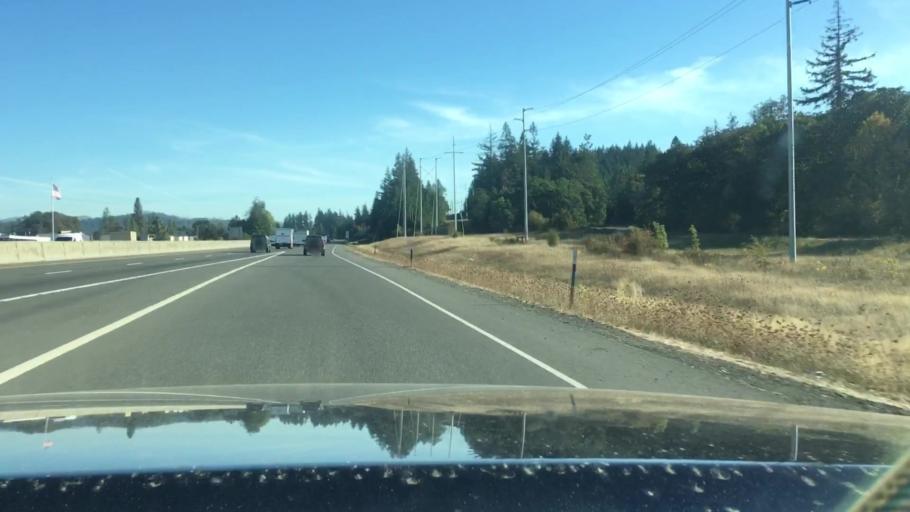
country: US
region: Oregon
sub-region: Lane County
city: Springfield
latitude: 44.0099
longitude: -123.0220
